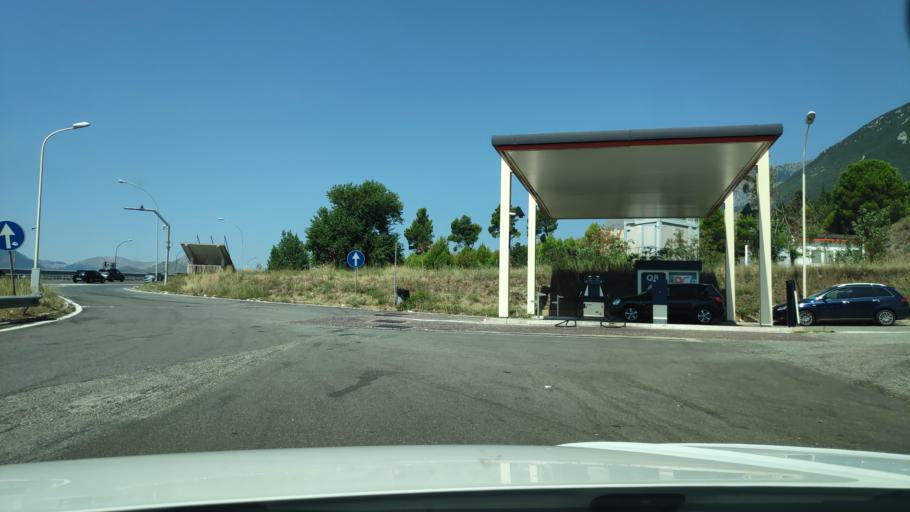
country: IT
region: Calabria
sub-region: Provincia di Cosenza
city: Frascineto
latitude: 39.8431
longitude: 16.2450
